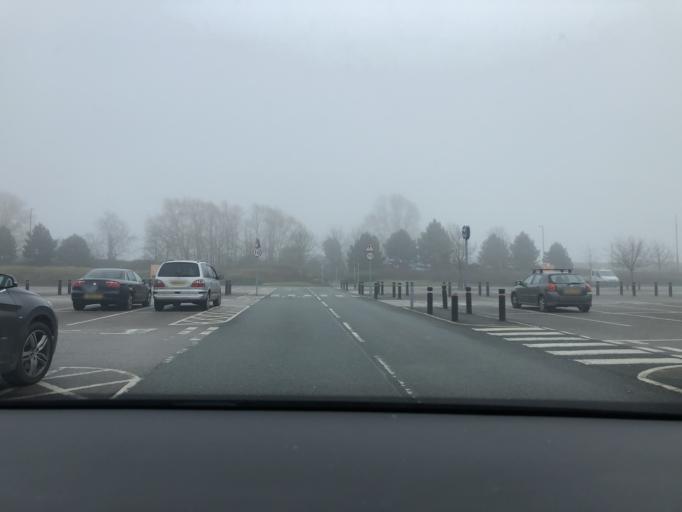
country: GB
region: England
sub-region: City and Borough of Salford
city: Eccles
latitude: 53.4717
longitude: -2.3495
